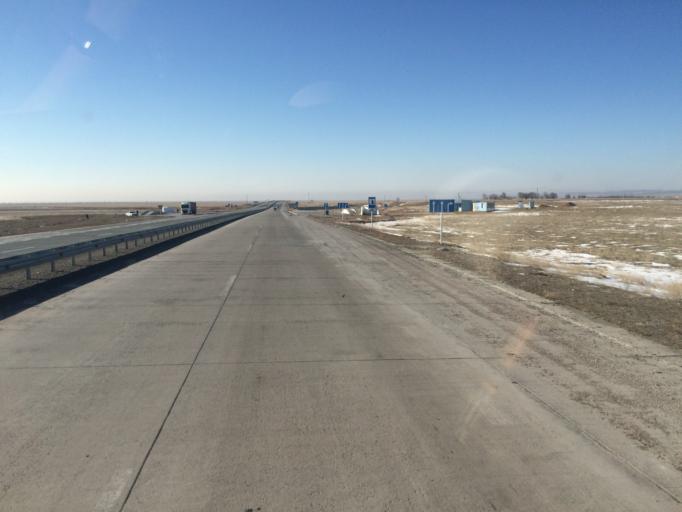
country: KZ
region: Zhambyl
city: Georgiyevka
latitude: 43.3426
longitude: 74.4202
